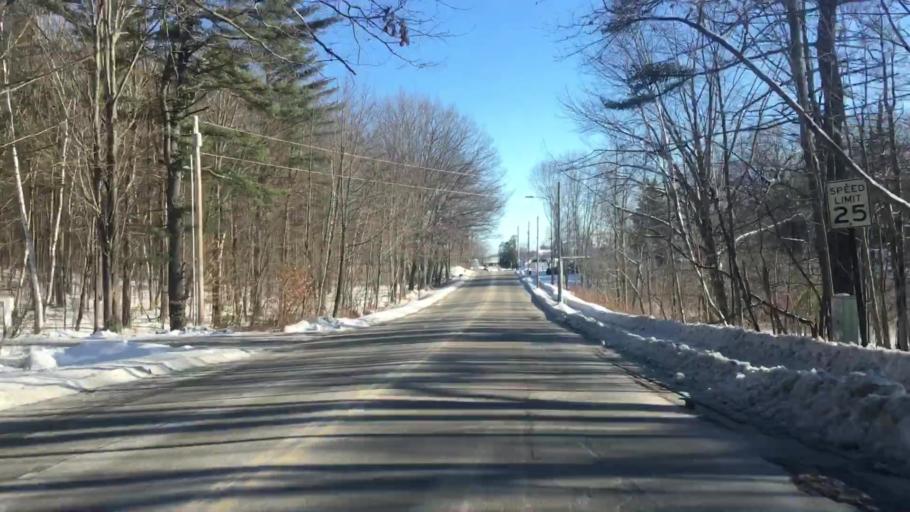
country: US
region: Maine
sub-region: Androscoggin County
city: Lewiston
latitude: 44.1063
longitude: -70.1785
